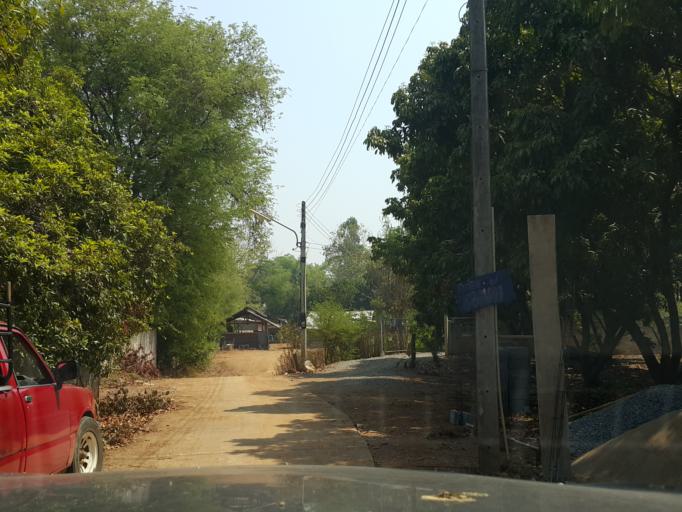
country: TH
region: Sukhothai
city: Thung Saliam
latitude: 17.3138
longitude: 99.5564
